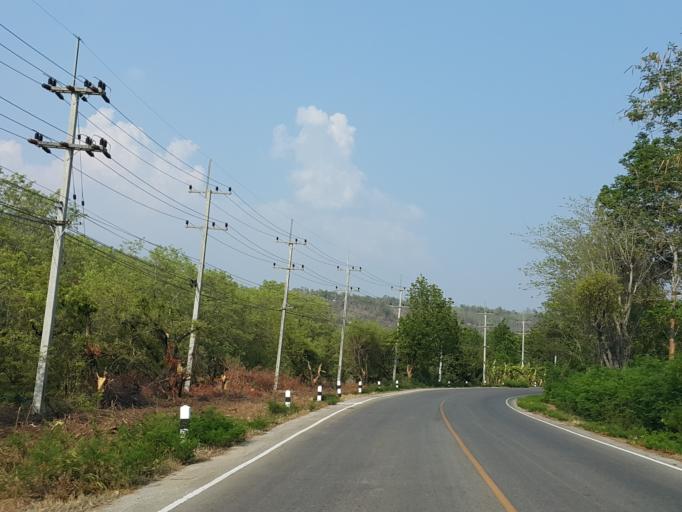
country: TH
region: Kanchanaburi
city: Sai Yok
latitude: 14.2207
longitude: 99.1630
